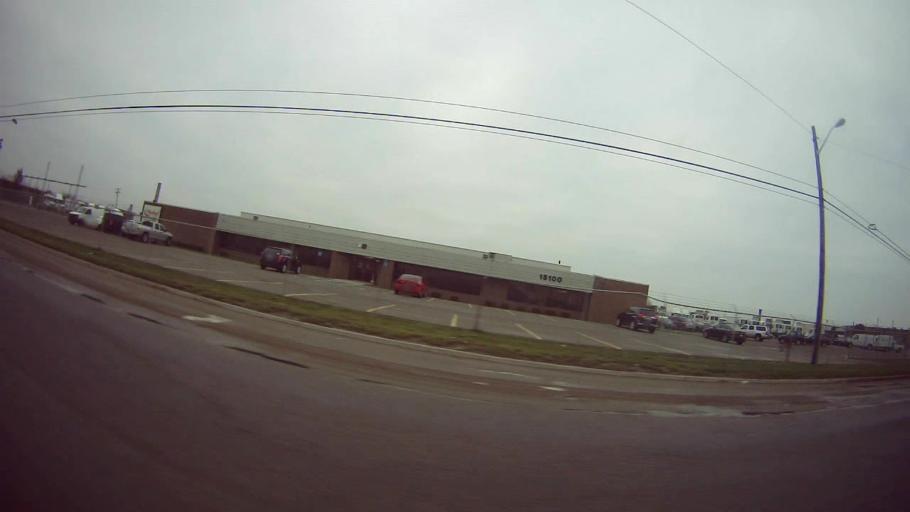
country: US
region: Michigan
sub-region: Wayne County
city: Highland Park
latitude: 42.4139
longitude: -83.0916
